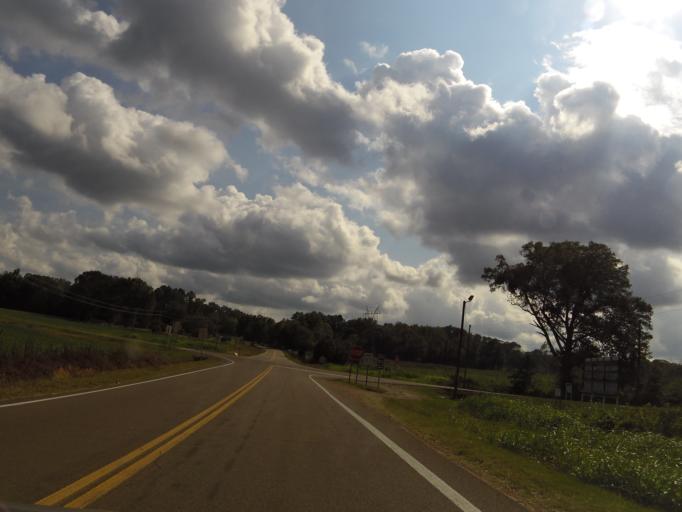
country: US
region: Mississippi
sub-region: Alcorn County
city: Farmington
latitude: 35.0703
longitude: -88.3931
